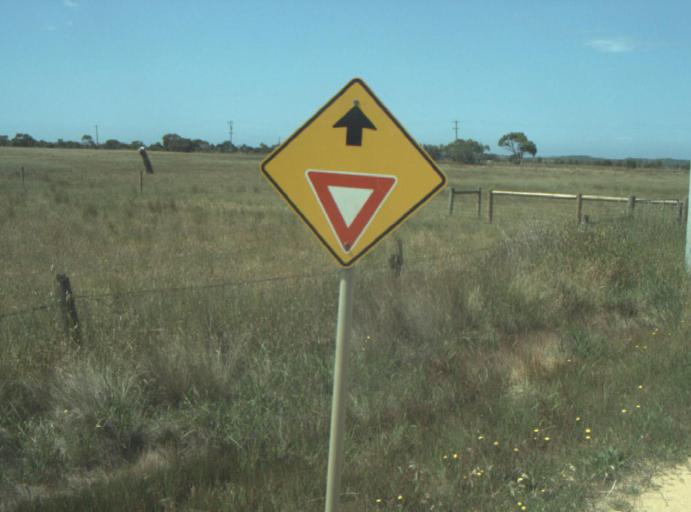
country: AU
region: Victoria
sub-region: Greater Geelong
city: Breakwater
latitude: -38.2642
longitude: 144.4047
